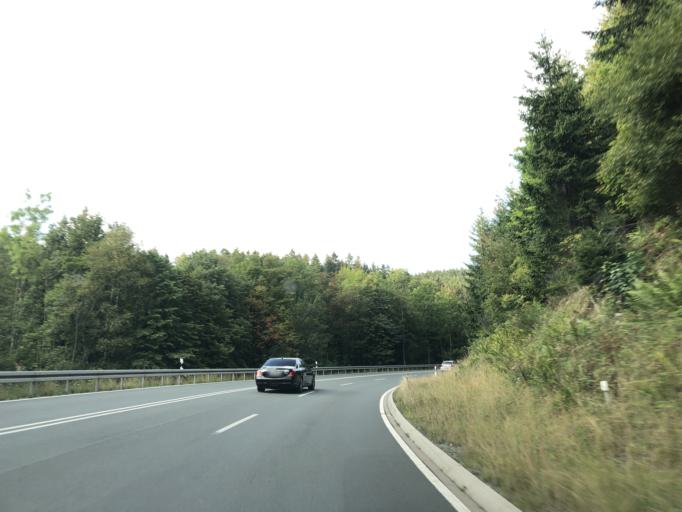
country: DE
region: North Rhine-Westphalia
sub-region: Regierungsbezirk Arnsberg
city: Winterberg
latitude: 51.1835
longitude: 8.5253
